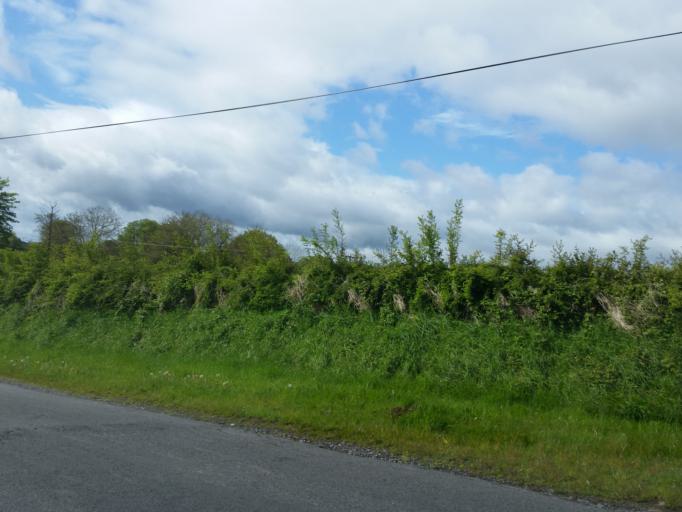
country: GB
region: Northern Ireland
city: Lisnaskea
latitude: 54.2545
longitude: -7.4213
